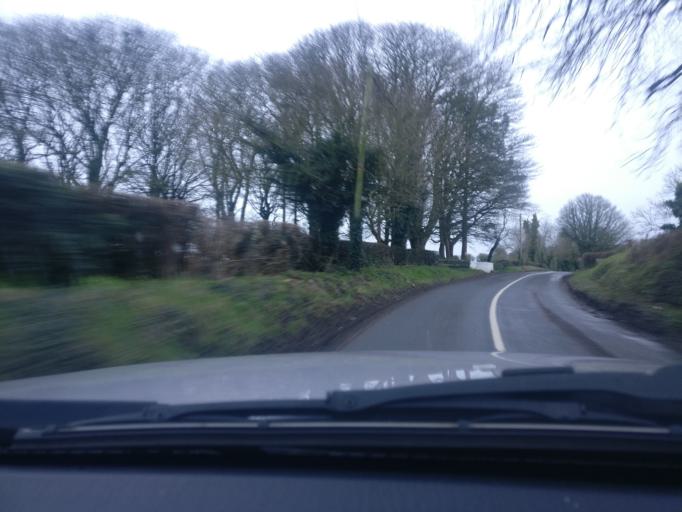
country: IE
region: Leinster
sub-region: An Mhi
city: Dunshaughlin
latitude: 53.4799
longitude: -6.6160
